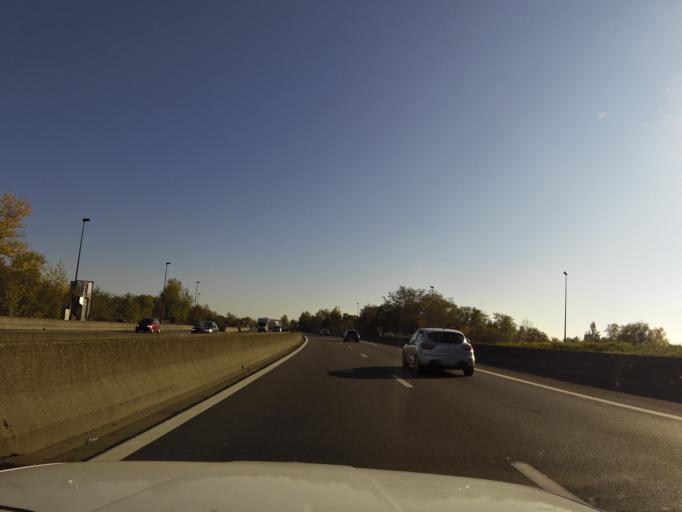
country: FR
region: Rhone-Alpes
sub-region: Departement du Rhone
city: Chassieu
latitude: 45.7521
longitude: 4.9856
